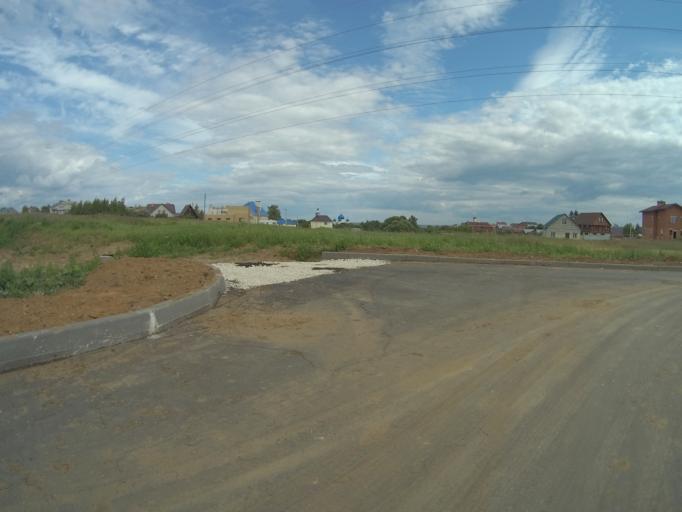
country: RU
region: Vladimir
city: Bogolyubovo
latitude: 56.1979
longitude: 40.5229
